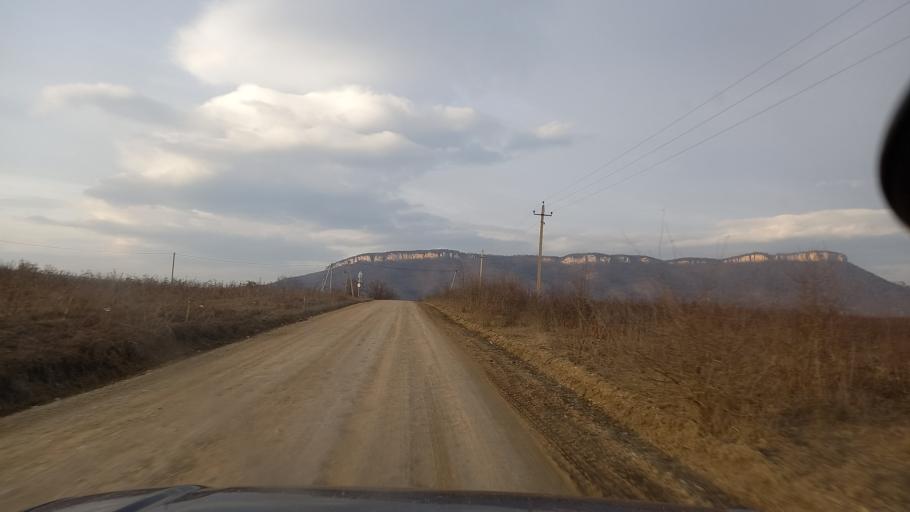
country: RU
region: Adygeya
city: Kamennomostskiy
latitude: 44.1966
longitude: 40.2525
